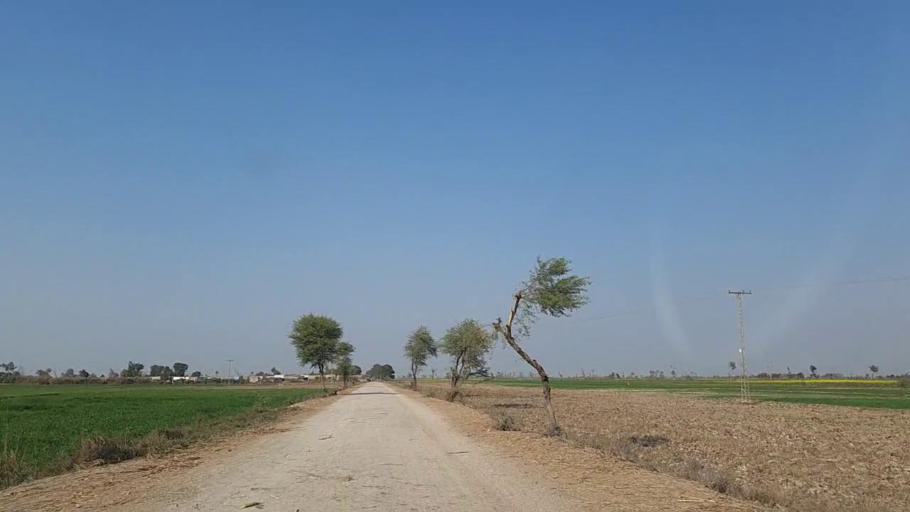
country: PK
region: Sindh
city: Daur
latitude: 26.4747
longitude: 68.2971
